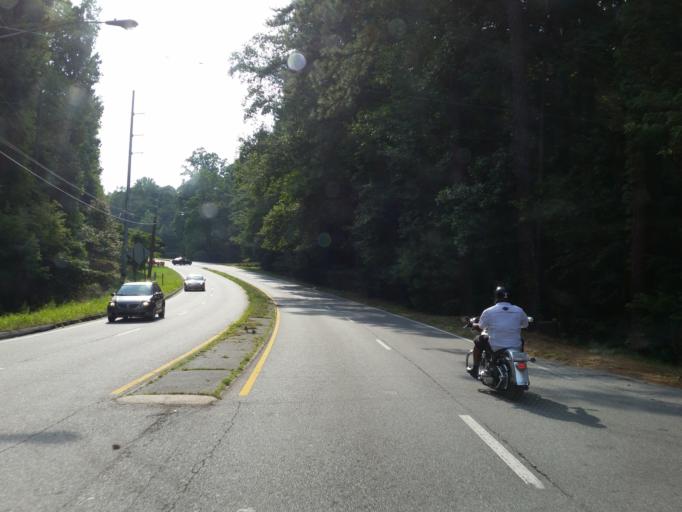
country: US
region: Georgia
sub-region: Cobb County
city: Vinings
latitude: 33.8400
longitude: -84.4103
